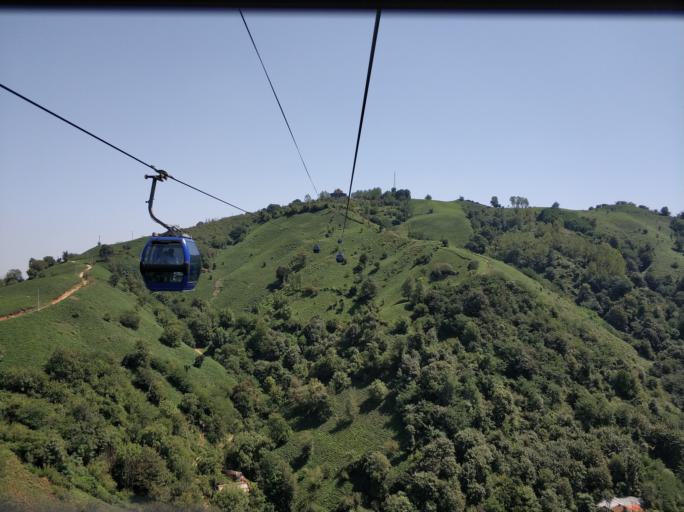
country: IR
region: Gilan
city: Lahijan
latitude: 37.1989
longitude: 50.0317
